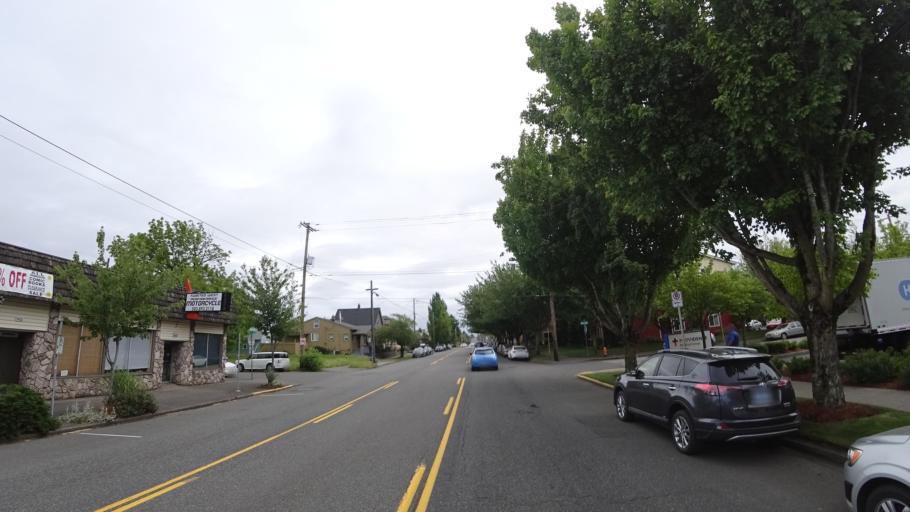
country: US
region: Oregon
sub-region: Multnomah County
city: Lents
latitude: 45.5265
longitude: -122.6079
